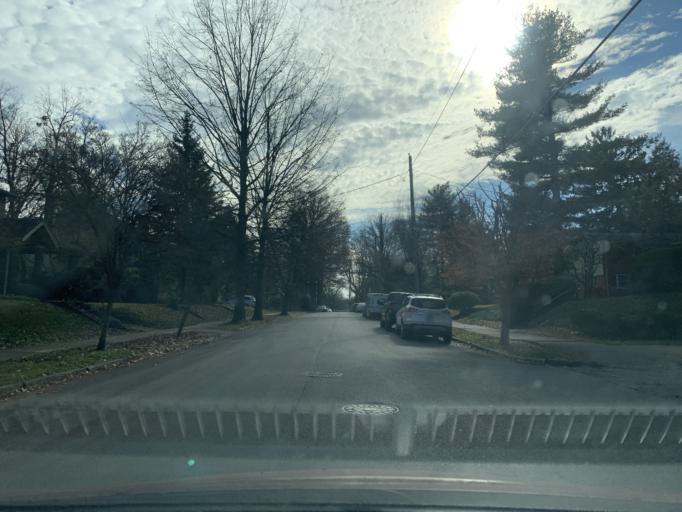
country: US
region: Kentucky
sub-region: Jefferson County
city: Indian Hills
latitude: 38.2531
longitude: -85.6963
